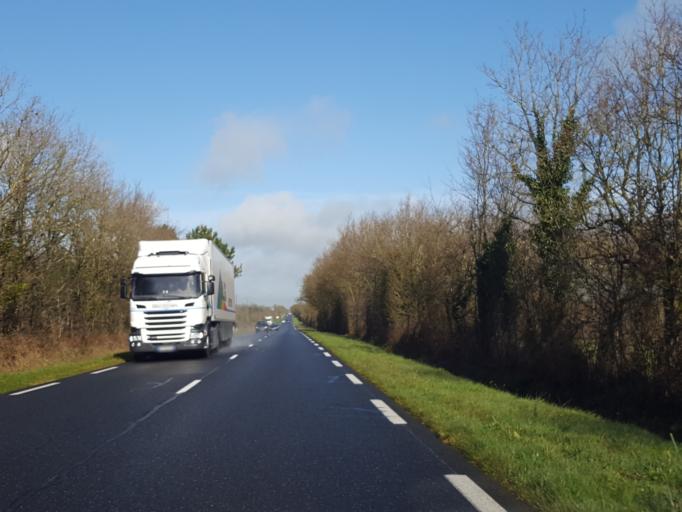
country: FR
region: Pays de la Loire
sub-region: Departement de la Vendee
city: Saligny
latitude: 46.8095
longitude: -1.4583
